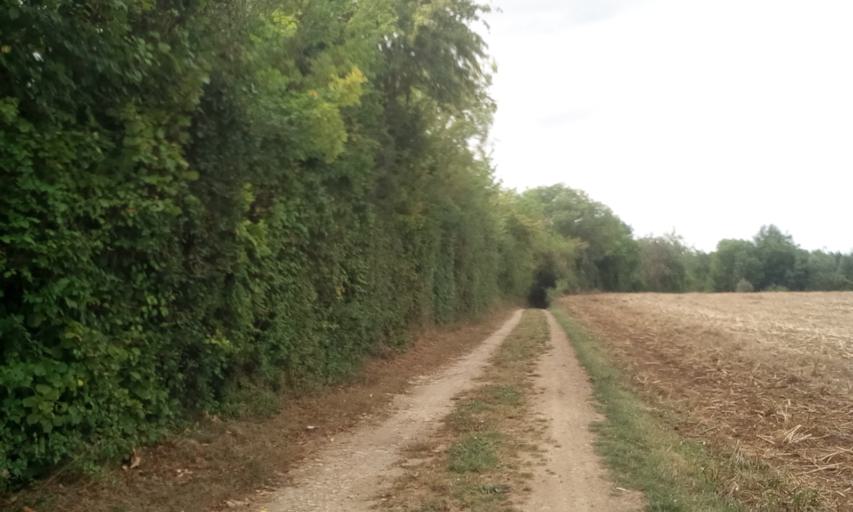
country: FR
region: Lower Normandy
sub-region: Departement du Calvados
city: Bellengreville
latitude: 49.1178
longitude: -0.2023
